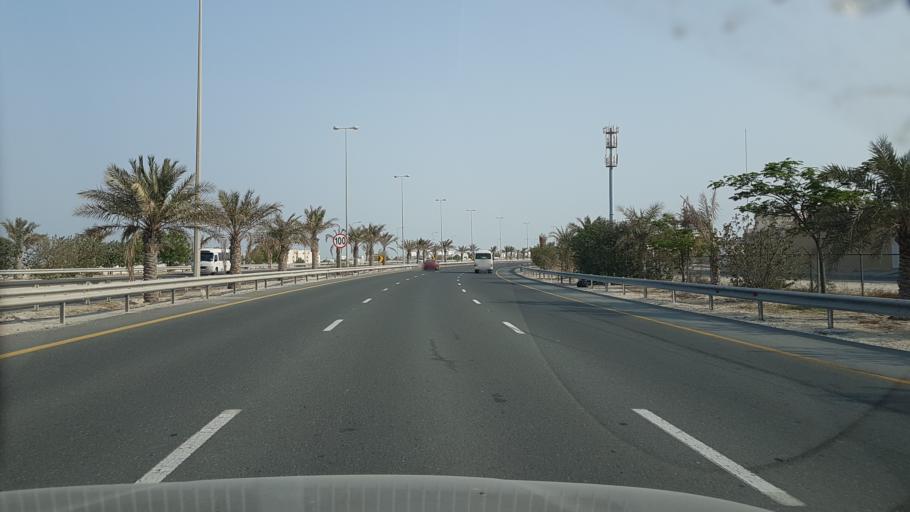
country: BH
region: Central Governorate
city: Madinat Hamad
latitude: 26.0926
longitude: 50.5395
